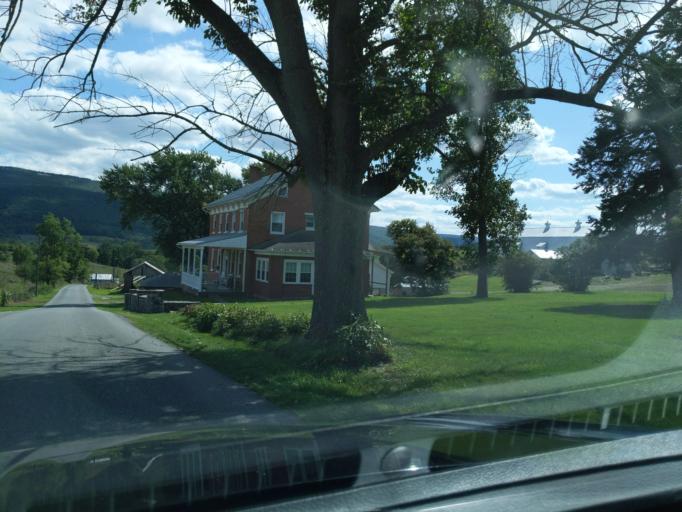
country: US
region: Pennsylvania
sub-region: Blair County
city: Tyrone
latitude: 40.6093
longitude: -78.2280
